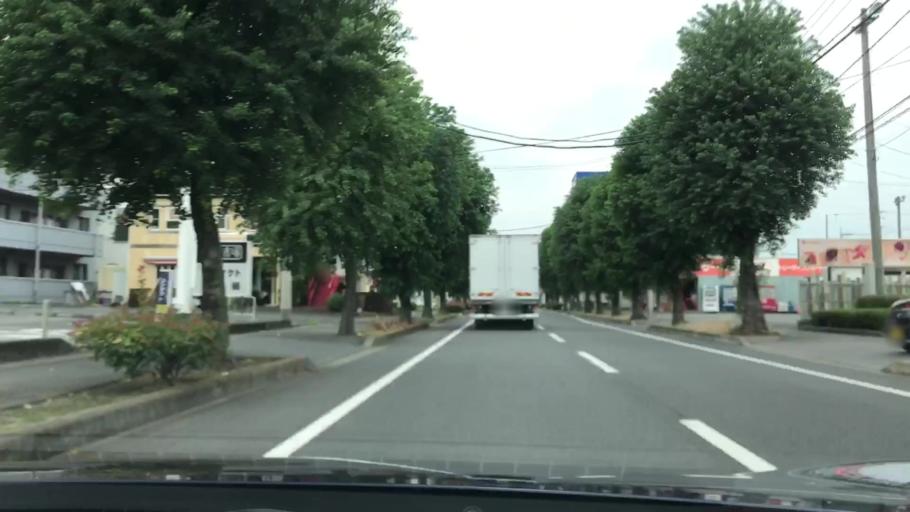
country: JP
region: Gunma
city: Isesaki
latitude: 36.3302
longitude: 139.1612
